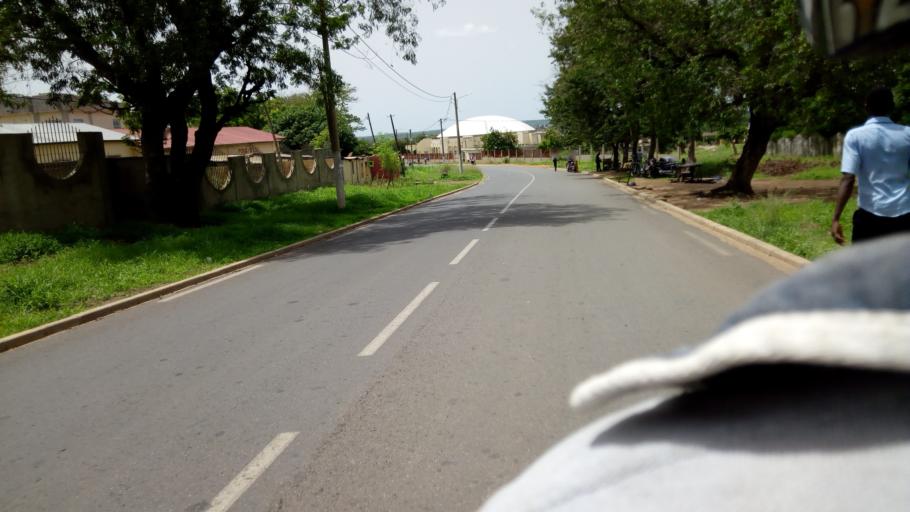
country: TG
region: Kara
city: Kara
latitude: 9.5498
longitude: 1.1792
